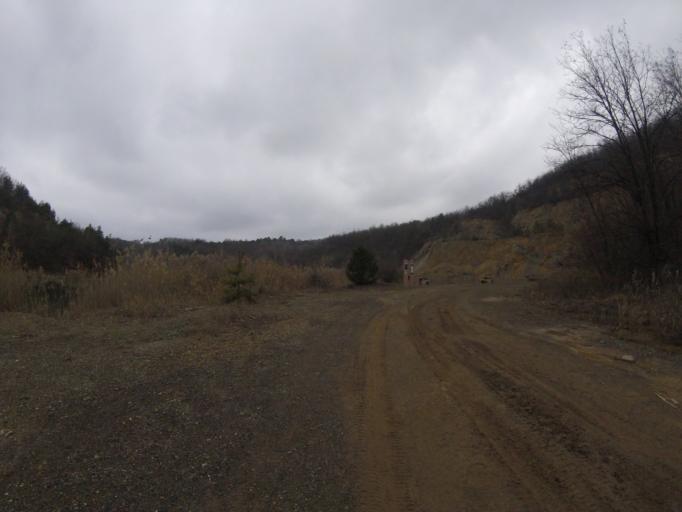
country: HU
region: Borsod-Abauj-Zemplen
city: Rudabanya
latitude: 48.3944
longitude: 20.6407
